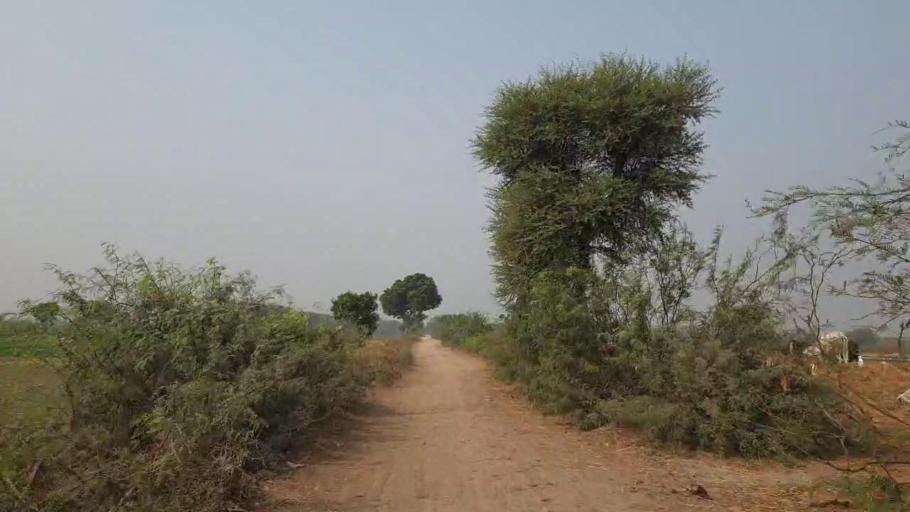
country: PK
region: Sindh
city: Tando Muhammad Khan
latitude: 25.2017
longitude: 68.5638
